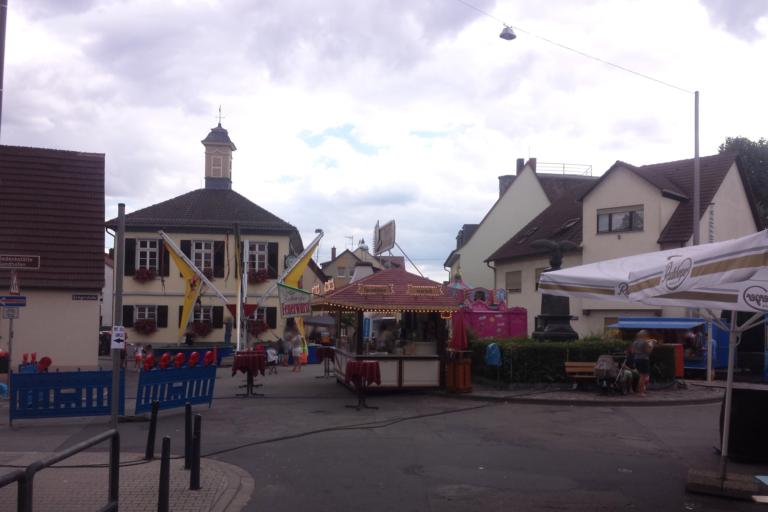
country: DE
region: Hesse
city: Lampertheim
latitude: 49.5451
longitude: 8.4429
